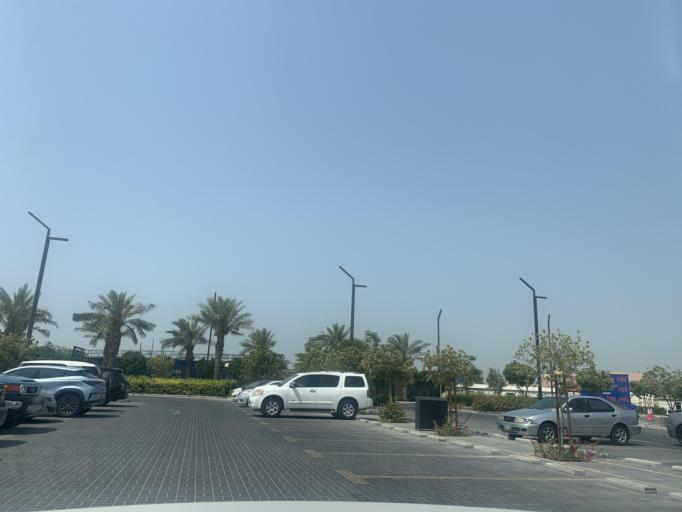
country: BH
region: Central Governorate
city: Madinat Hamad
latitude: 26.1602
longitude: 50.4695
